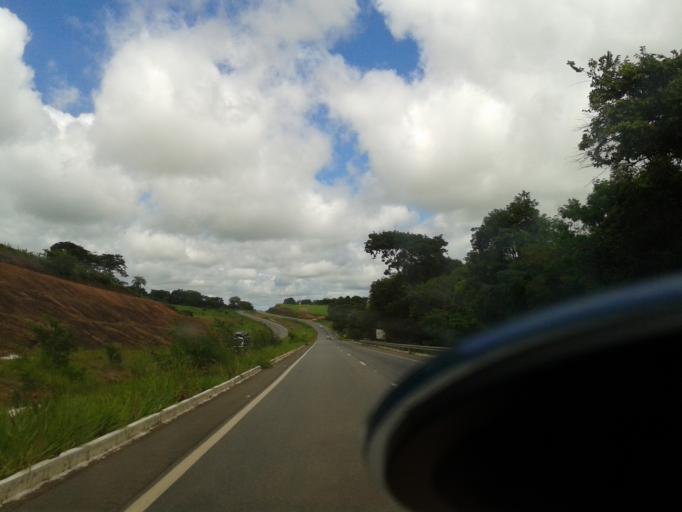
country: BR
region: Goias
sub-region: Itaberai
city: Itaberai
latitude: -16.1519
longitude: -49.6307
